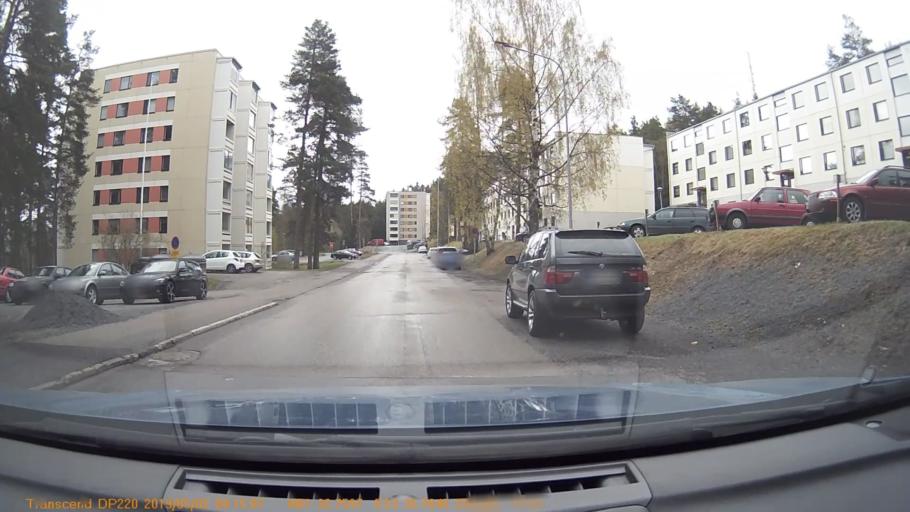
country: FI
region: Pirkanmaa
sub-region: Tampere
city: Yloejaervi
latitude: 61.5460
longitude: 23.5961
